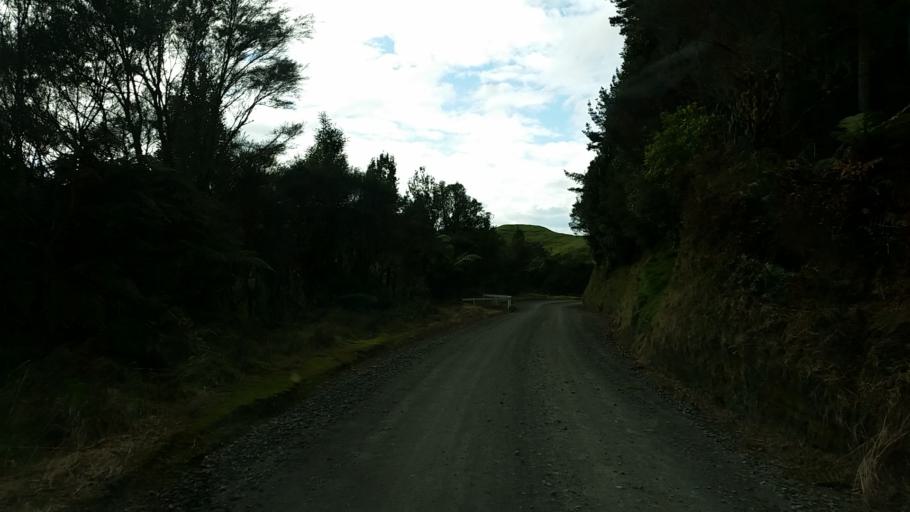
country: NZ
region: Taranaki
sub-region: New Plymouth District
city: Waitara
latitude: -39.1589
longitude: 174.5524
